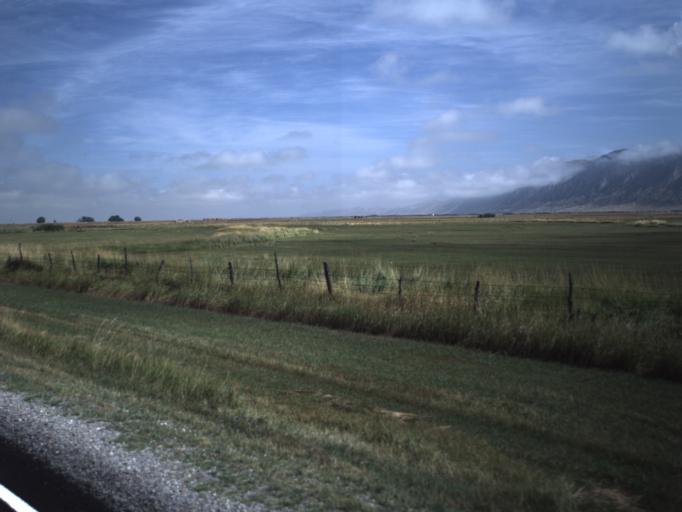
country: US
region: Utah
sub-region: Rich County
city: Randolph
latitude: 41.6187
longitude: -111.1793
